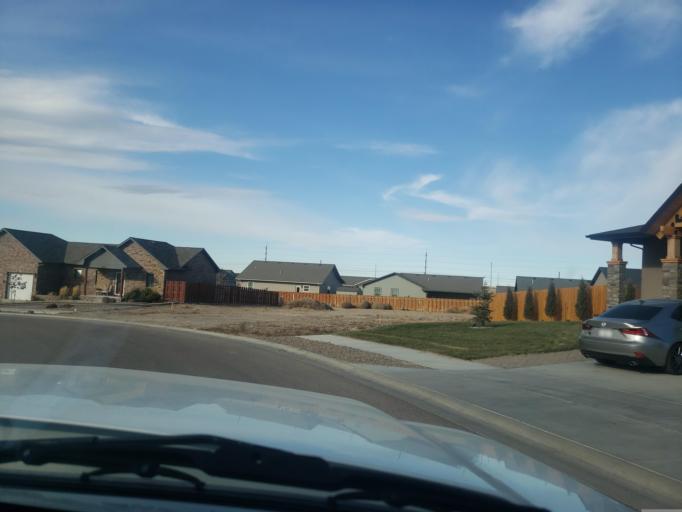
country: US
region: Kansas
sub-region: Finney County
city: Garden City
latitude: 37.9877
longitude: -100.8229
